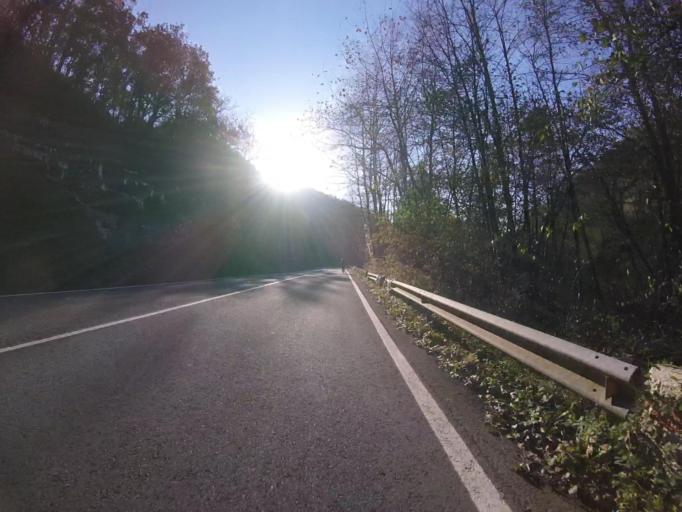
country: ES
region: Navarre
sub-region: Provincia de Navarra
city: Lesaka
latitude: 43.2485
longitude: -1.6707
